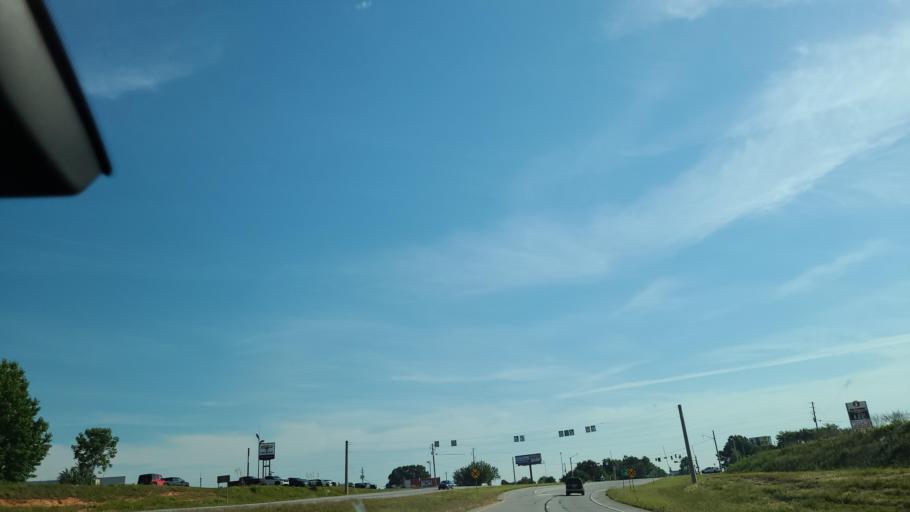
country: US
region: Georgia
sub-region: Jackson County
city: Commerce
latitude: 34.1812
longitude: -83.4420
